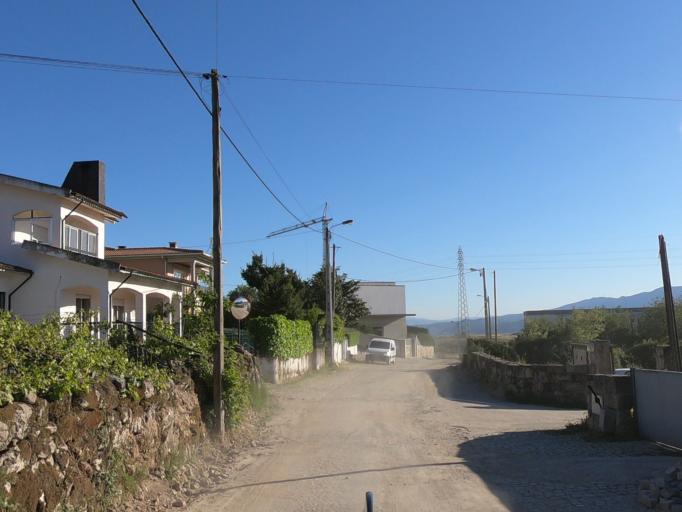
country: PT
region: Vila Real
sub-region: Vila Real
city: Vila Real
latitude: 41.3270
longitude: -7.6931
